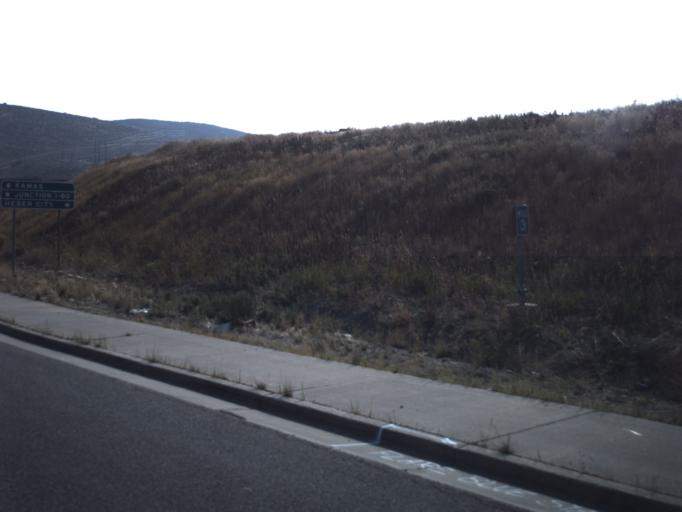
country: US
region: Utah
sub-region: Summit County
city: Park City
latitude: 40.6822
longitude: -111.4645
